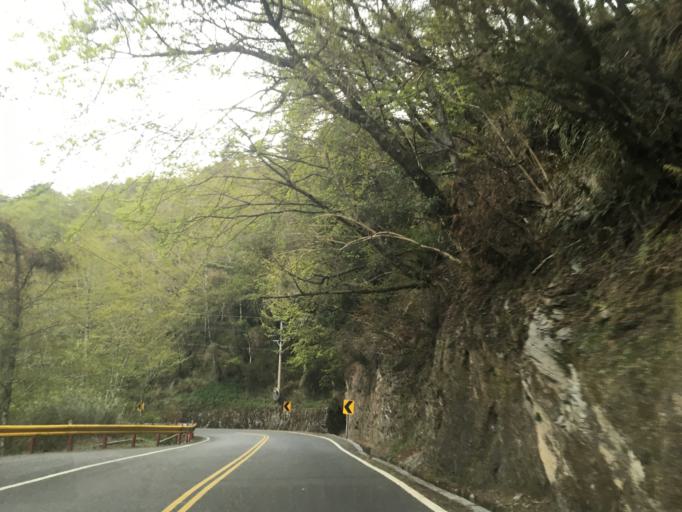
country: TW
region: Taiwan
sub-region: Hualien
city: Hualian
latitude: 24.1805
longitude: 121.3152
